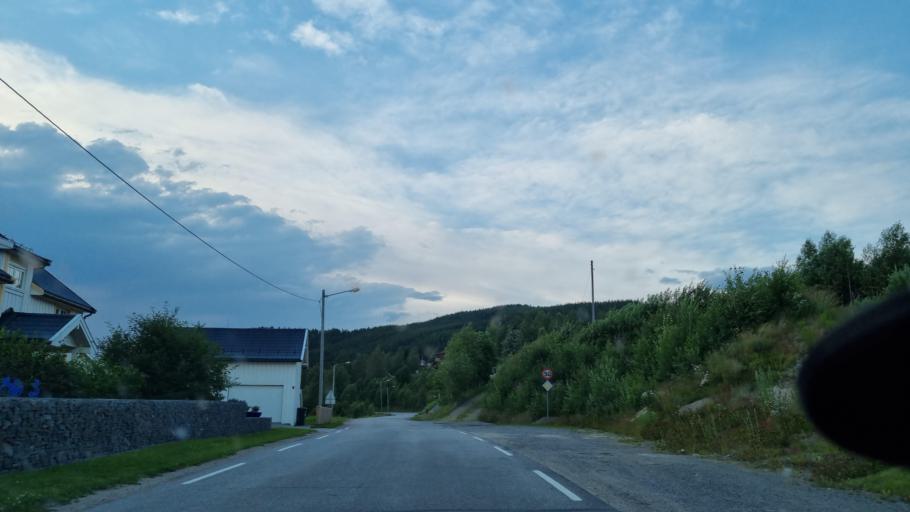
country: NO
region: Hedmark
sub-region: Trysil
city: Innbygda
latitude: 61.3191
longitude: 12.2599
